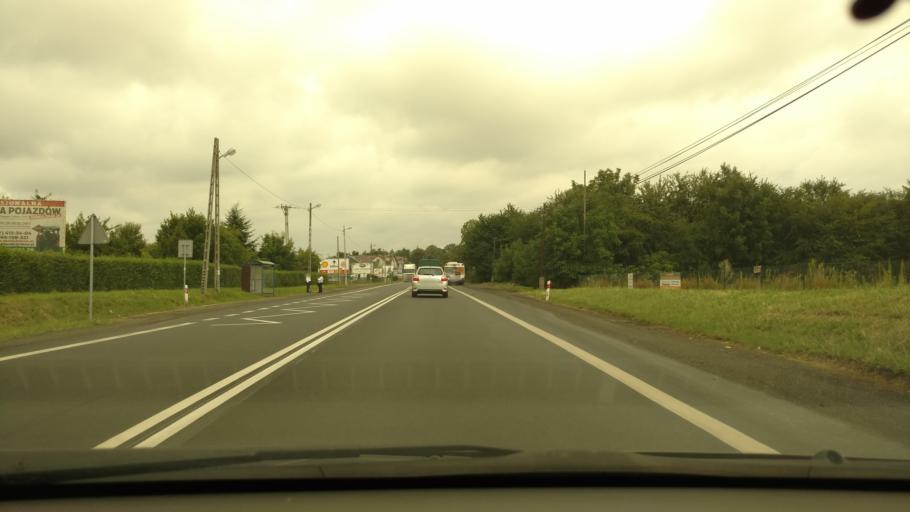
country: PL
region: Lesser Poland Voivodeship
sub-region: Powiat krakowski
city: Zielonki
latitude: 50.1096
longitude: 19.9658
